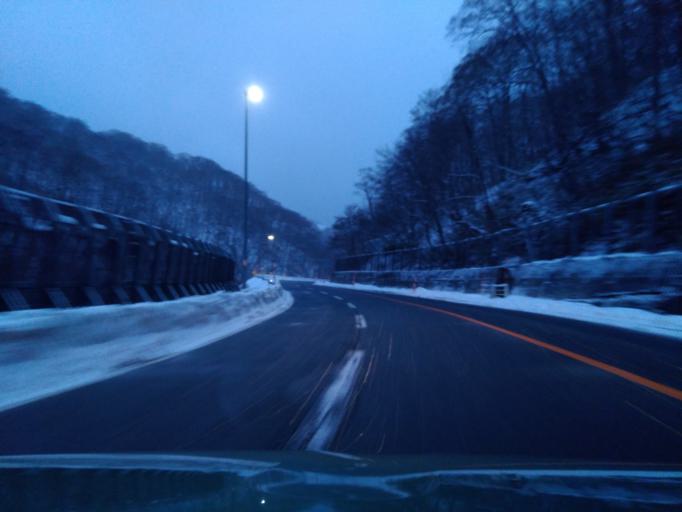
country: JP
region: Iwate
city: Shizukuishi
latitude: 39.7211
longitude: 140.8253
